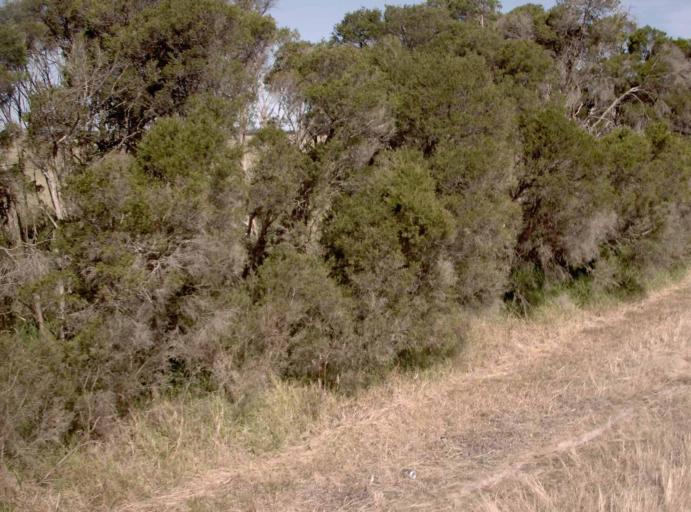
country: AU
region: Victoria
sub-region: Wellington
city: Sale
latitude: -38.3183
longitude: 147.1564
